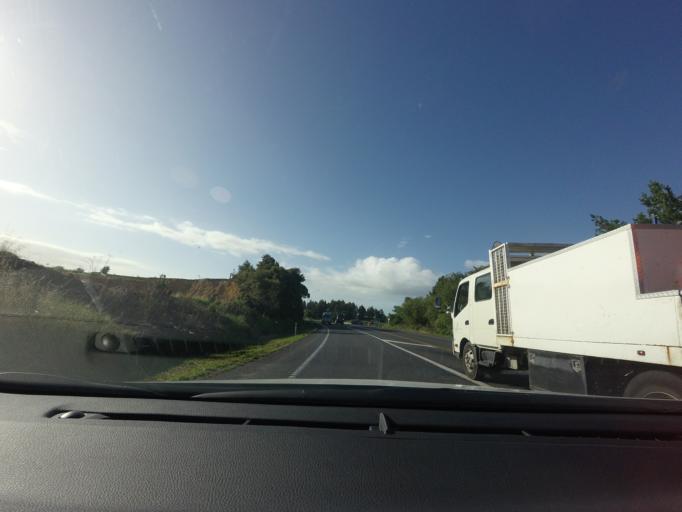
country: NZ
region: Waikato
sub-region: Hauraki District
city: Ngatea
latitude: -37.4720
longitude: 175.5097
